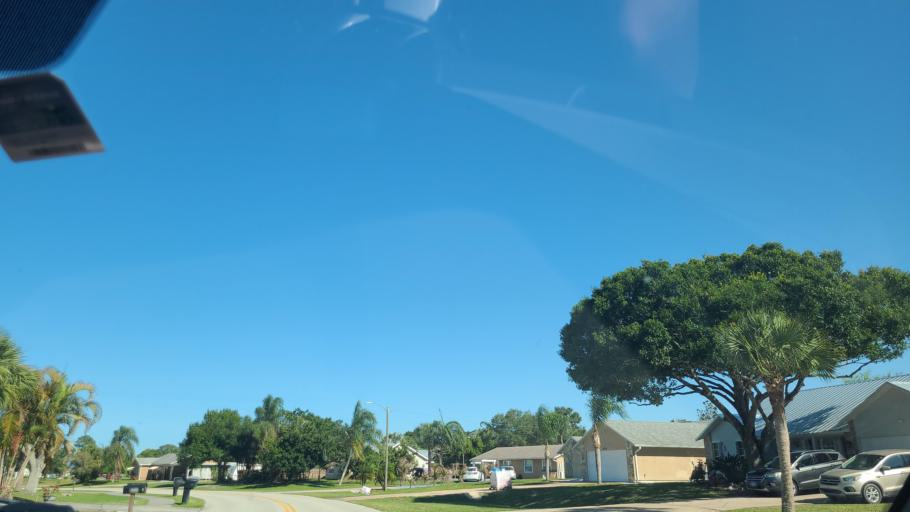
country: US
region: Florida
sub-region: Indian River County
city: Sebastian
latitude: 27.7574
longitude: -80.4841
